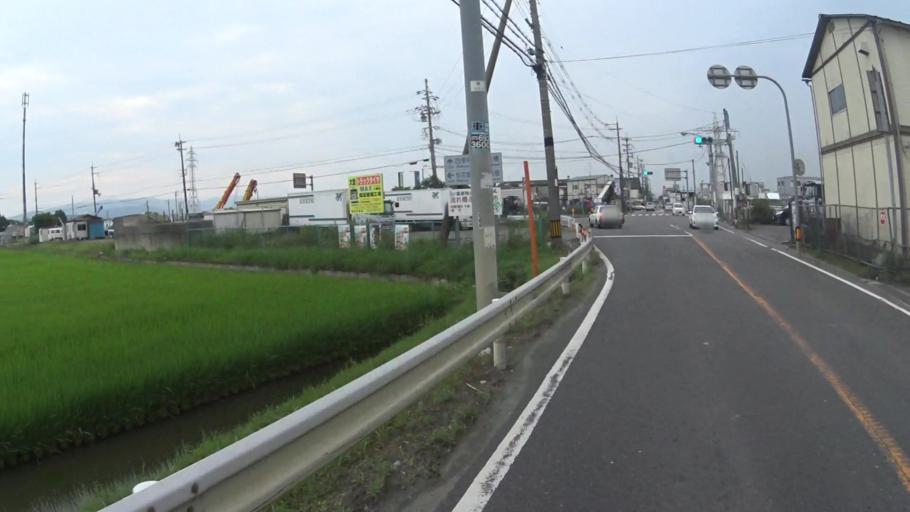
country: JP
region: Kyoto
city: Tanabe
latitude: 34.8284
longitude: 135.7580
